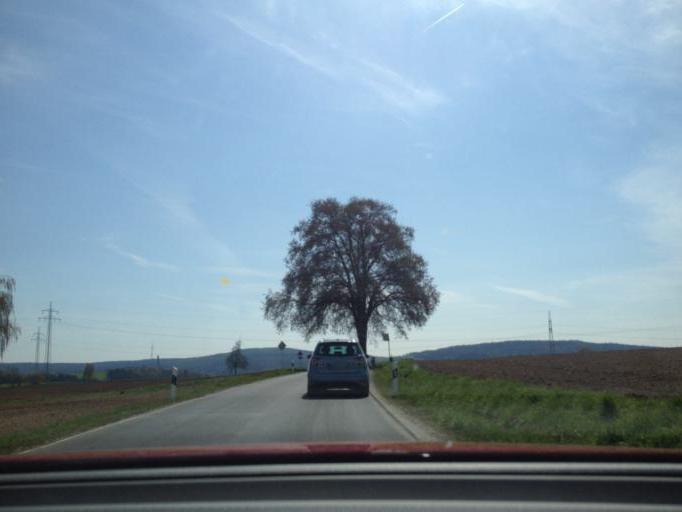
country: DE
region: Bavaria
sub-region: Upper Franconia
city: Arzberg
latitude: 50.0656
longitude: 12.1562
